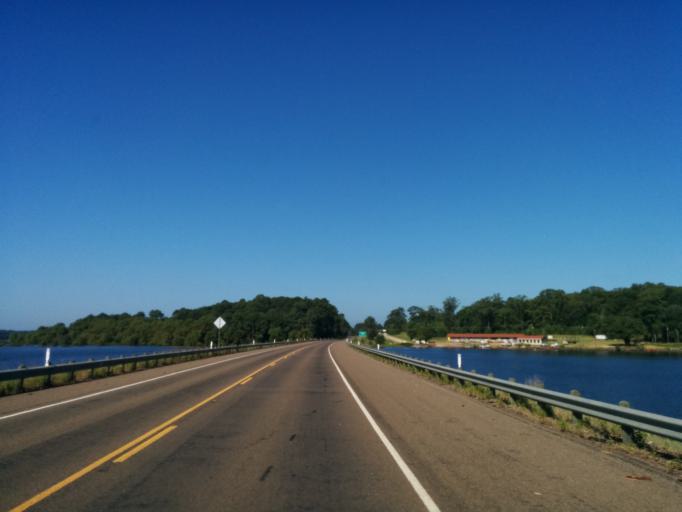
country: US
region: Texas
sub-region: Sabine County
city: Milam
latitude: 31.4647
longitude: -93.7480
